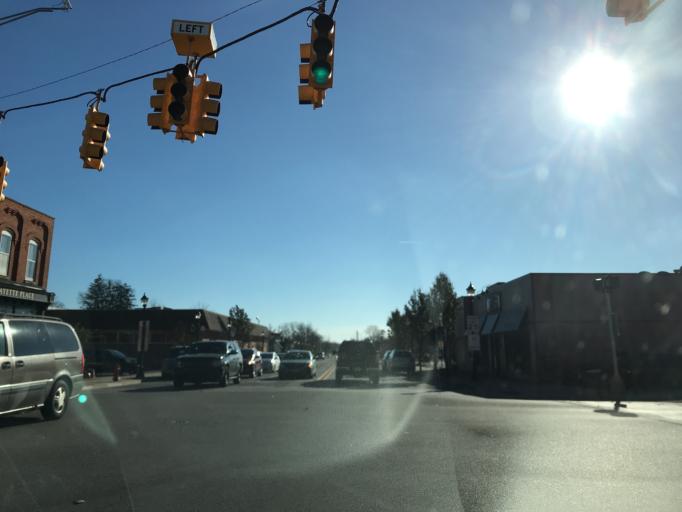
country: US
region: Michigan
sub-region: Oakland County
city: South Lyon
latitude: 42.4607
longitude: -83.6516
